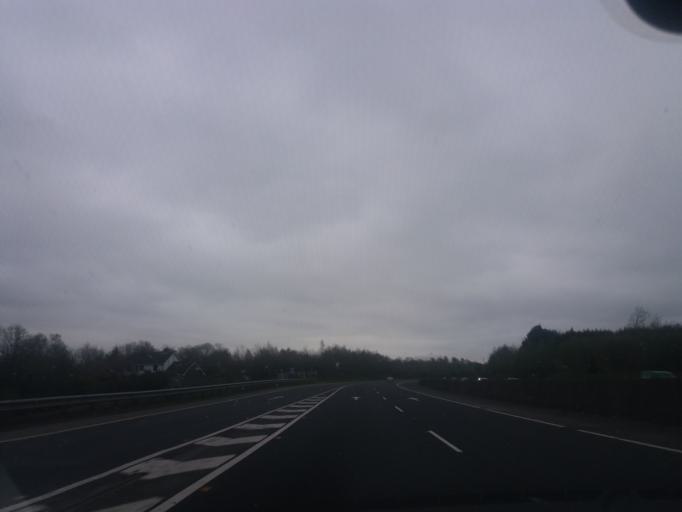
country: IE
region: Munster
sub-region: County Limerick
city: Annacotty
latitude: 52.6706
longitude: -8.5155
